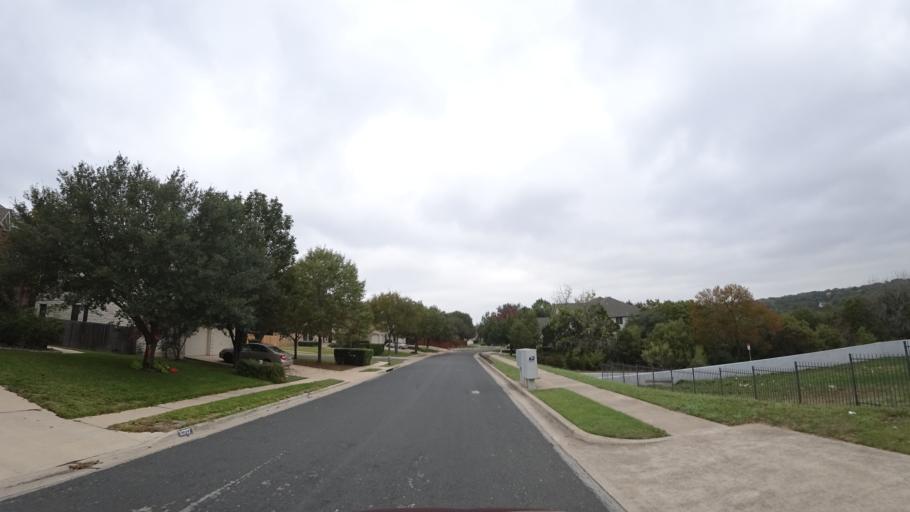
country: US
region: Texas
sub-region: Williamson County
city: Anderson Mill
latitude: 30.4365
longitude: -97.8161
